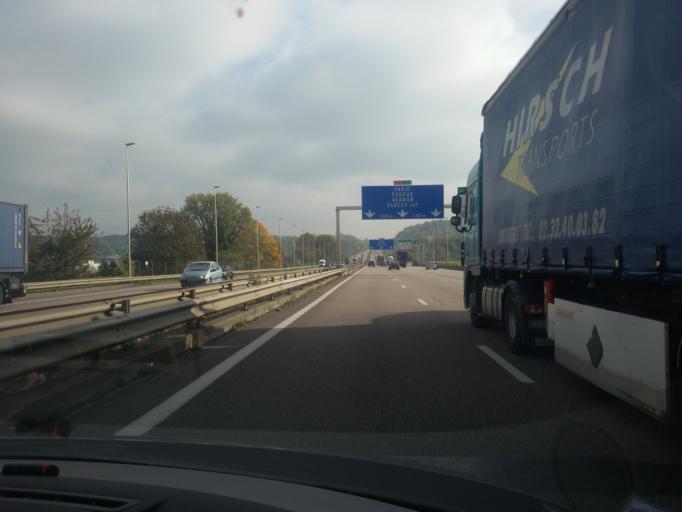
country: FR
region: Haute-Normandie
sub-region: Departement de la Seine-Maritime
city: Oissel
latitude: 49.3302
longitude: 1.0859
